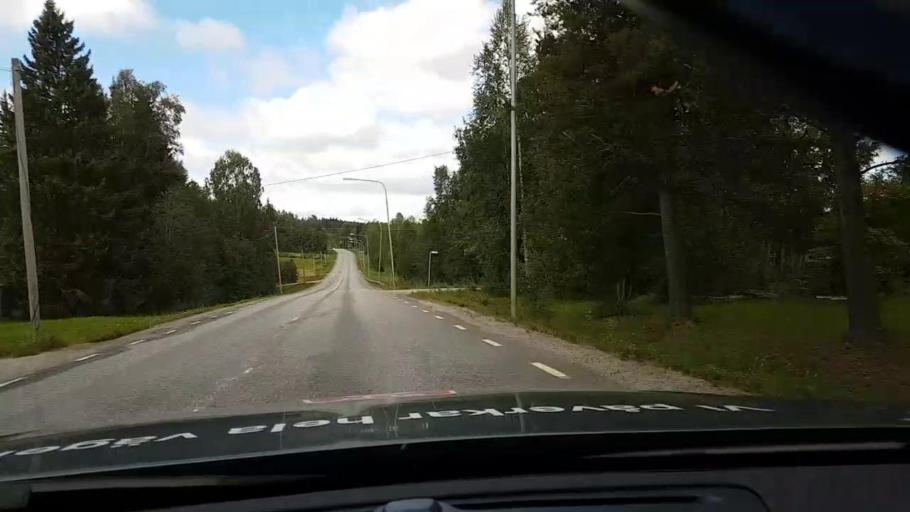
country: SE
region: Vaesternorrland
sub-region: OErnskoeldsviks Kommun
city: Bredbyn
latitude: 63.4854
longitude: 18.0867
